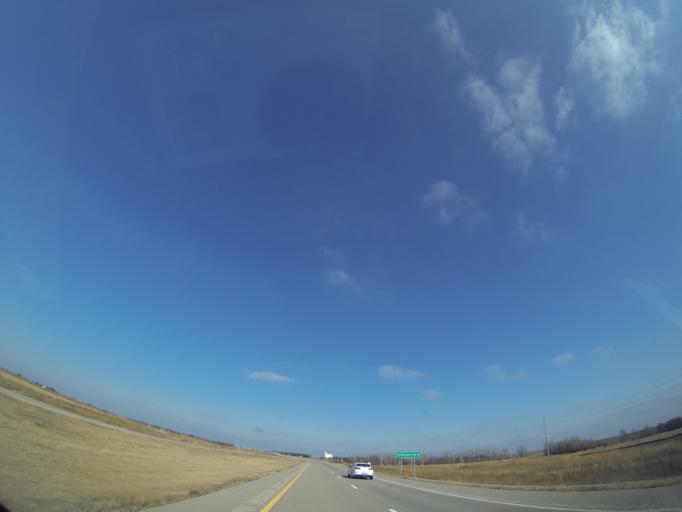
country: US
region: Kansas
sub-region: McPherson County
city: Inman
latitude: 38.2156
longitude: -97.7905
